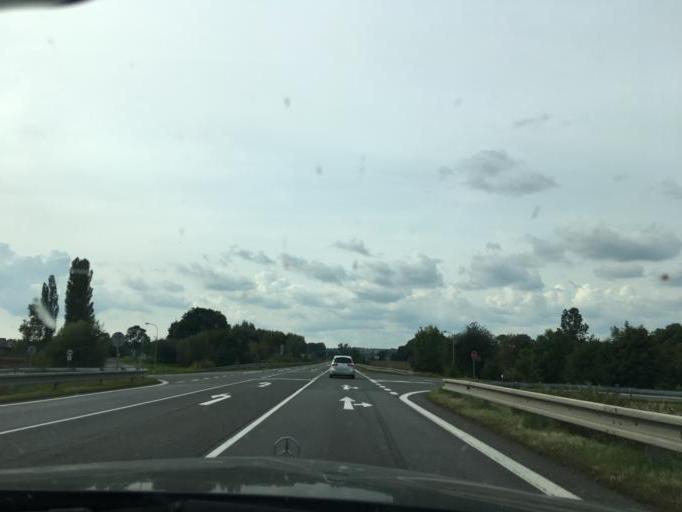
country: CZ
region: Kralovehradecky
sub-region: Okres Nachod
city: Ceska Skalice
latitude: 50.3868
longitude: 16.0282
